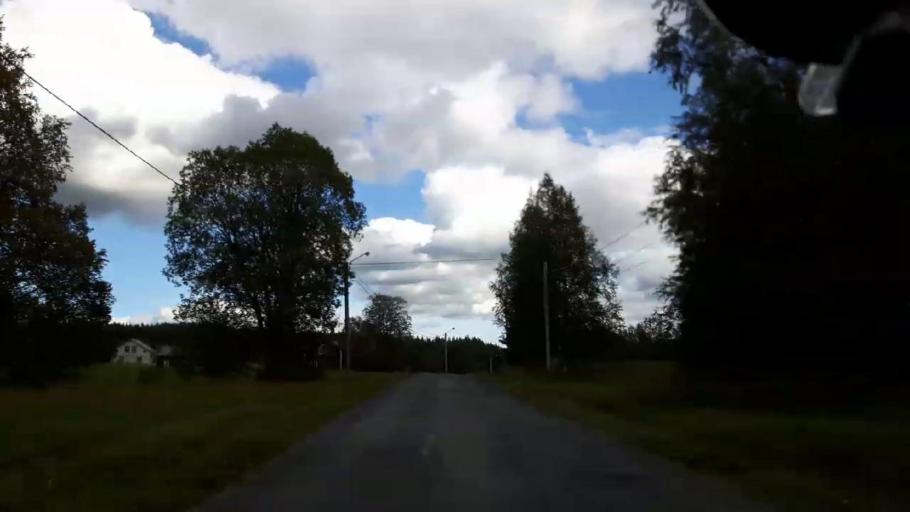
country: SE
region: Jaemtland
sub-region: Stroemsunds Kommun
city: Stroemsund
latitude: 63.4194
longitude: 15.8414
